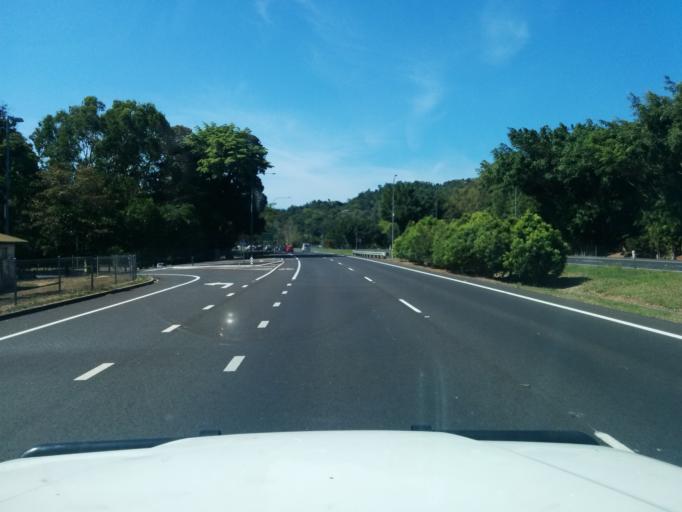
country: AU
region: Queensland
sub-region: Cairns
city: Redlynch
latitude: -16.8996
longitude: 145.7094
